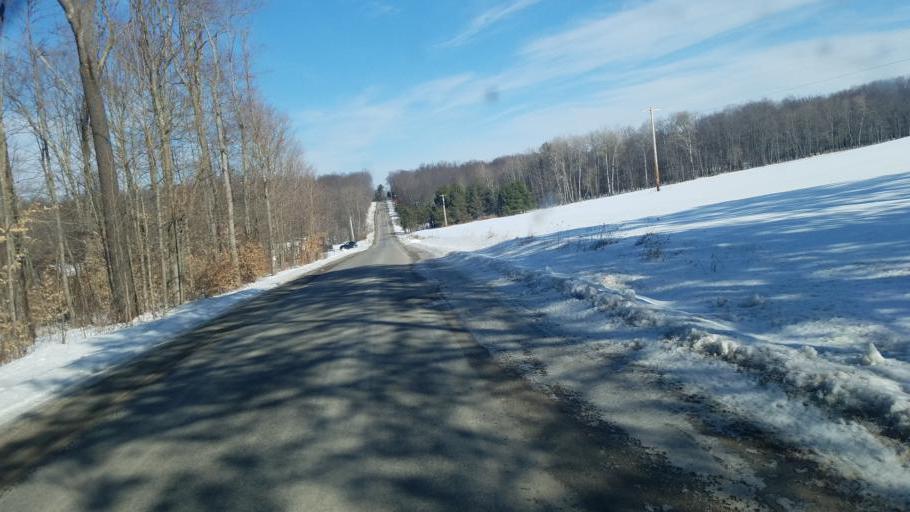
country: US
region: New York
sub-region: Allegany County
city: Andover
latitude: 42.0811
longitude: -77.7717
